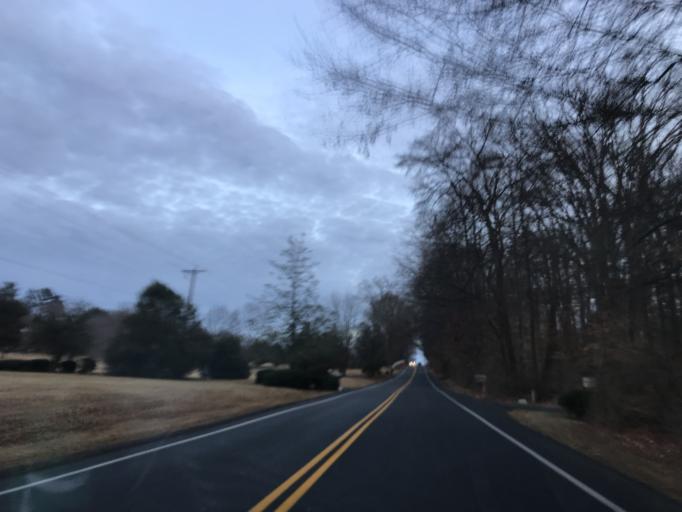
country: US
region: Maryland
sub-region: Harford County
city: Bel Air South
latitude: 39.4928
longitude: -76.3146
